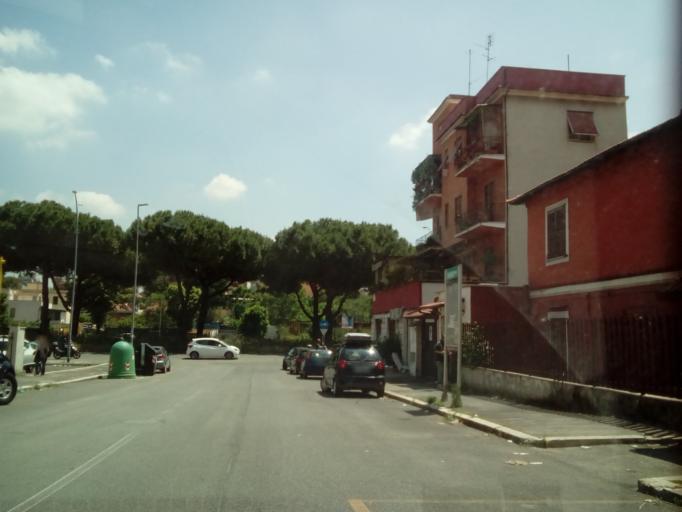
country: IT
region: Latium
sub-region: Citta metropolitana di Roma Capitale
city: Rome
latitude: 41.8824
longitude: 12.5723
